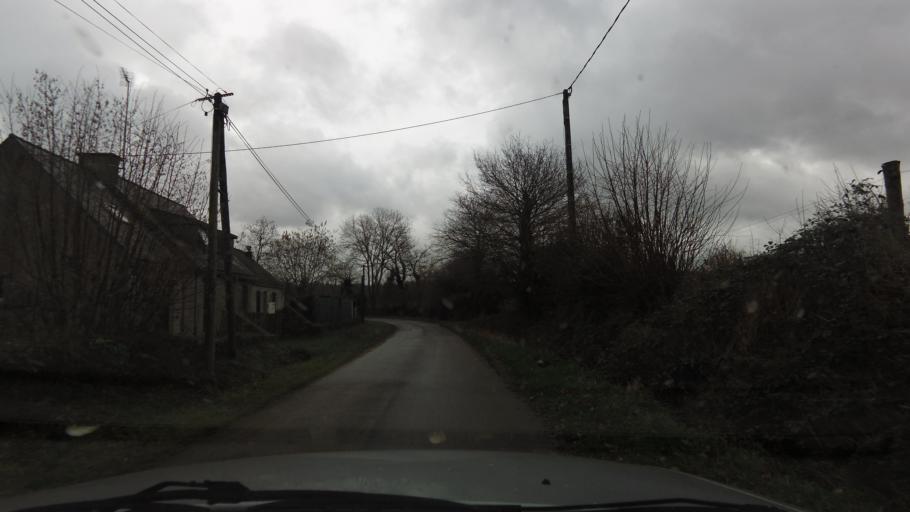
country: FR
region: Brittany
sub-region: Departement du Morbihan
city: Molac
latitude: 47.7699
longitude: -2.4594
